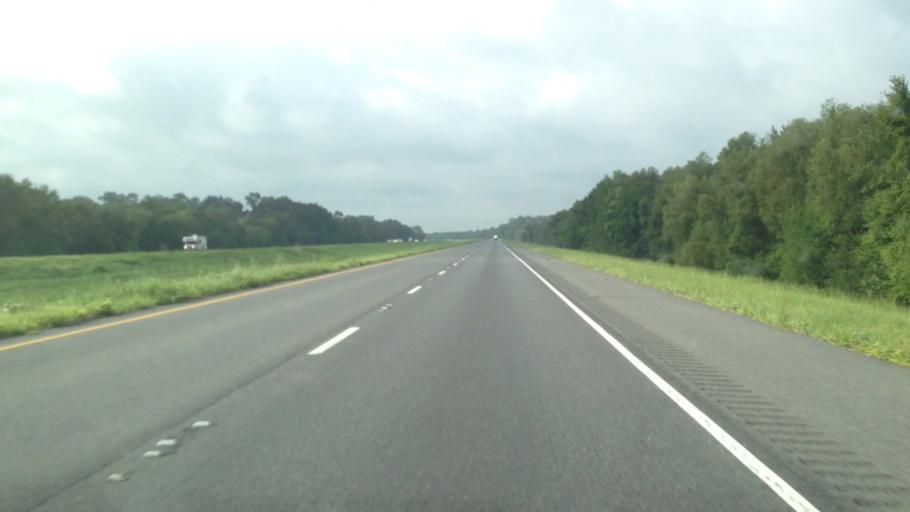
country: US
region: Louisiana
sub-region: Saint Landry Parish
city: Opelousas
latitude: 30.6809
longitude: -92.0766
